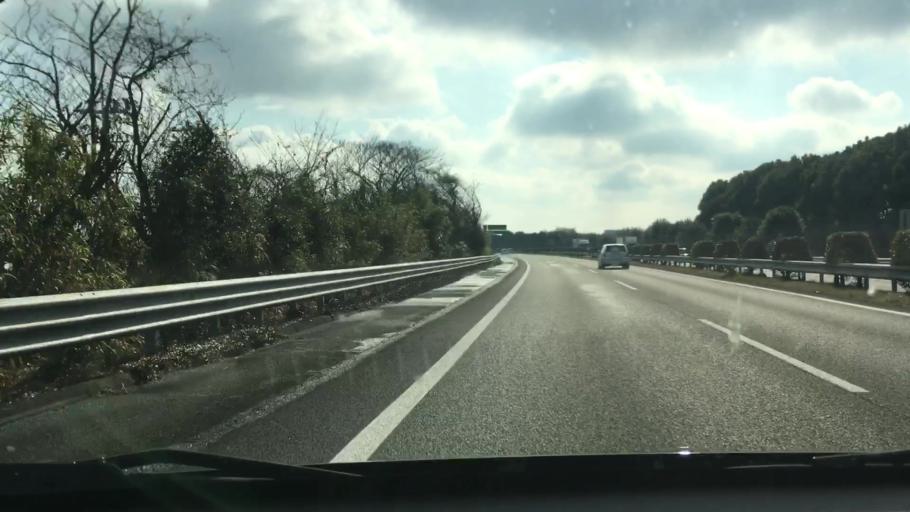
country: JP
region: Kumamoto
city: Kumamoto
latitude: 32.7996
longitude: 130.7909
